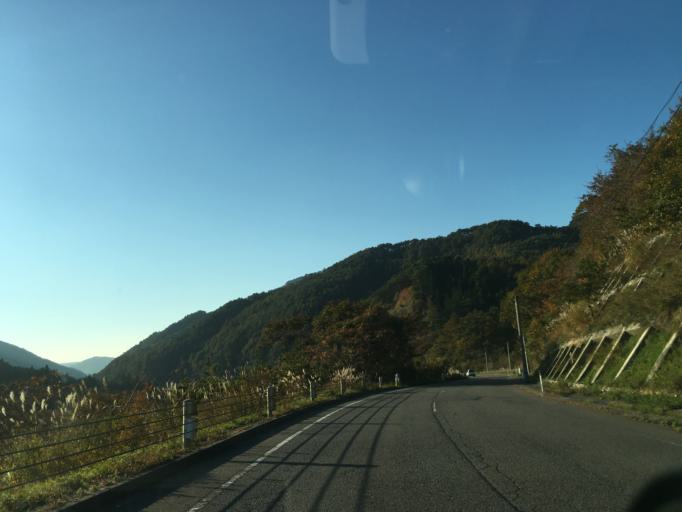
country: JP
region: Fukushima
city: Inawashiro
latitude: 37.3934
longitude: 140.1798
